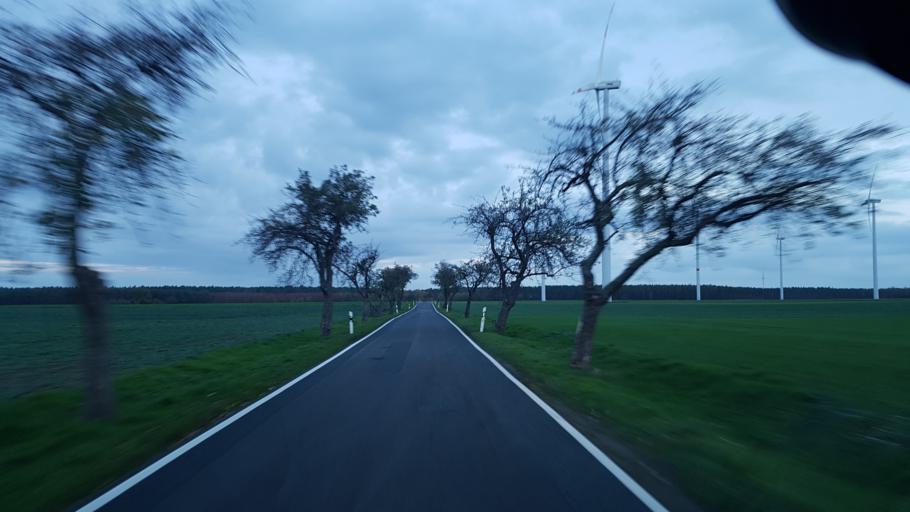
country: DE
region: Brandenburg
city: Muhlberg
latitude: 51.4656
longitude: 13.2476
